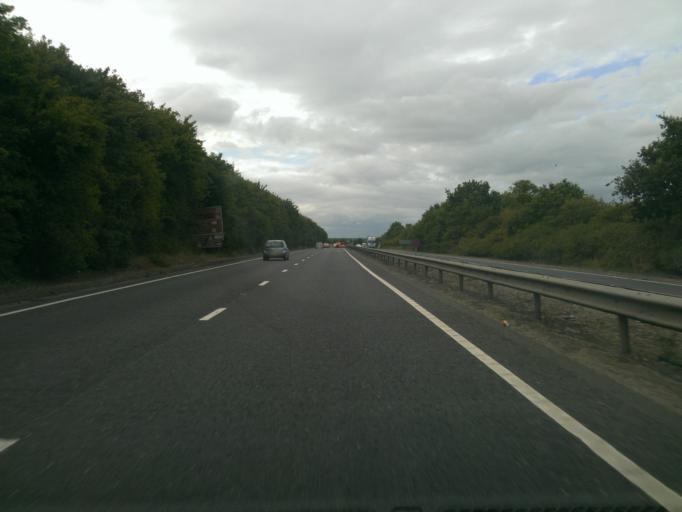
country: GB
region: England
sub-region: Essex
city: Rayne
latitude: 51.8772
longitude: 0.5847
